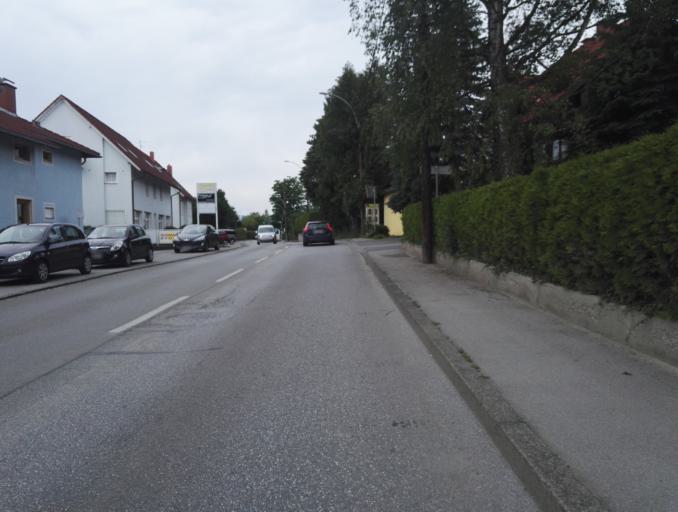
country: AT
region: Styria
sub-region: Graz Stadt
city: Mariatrost
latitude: 47.0782
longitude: 15.4871
